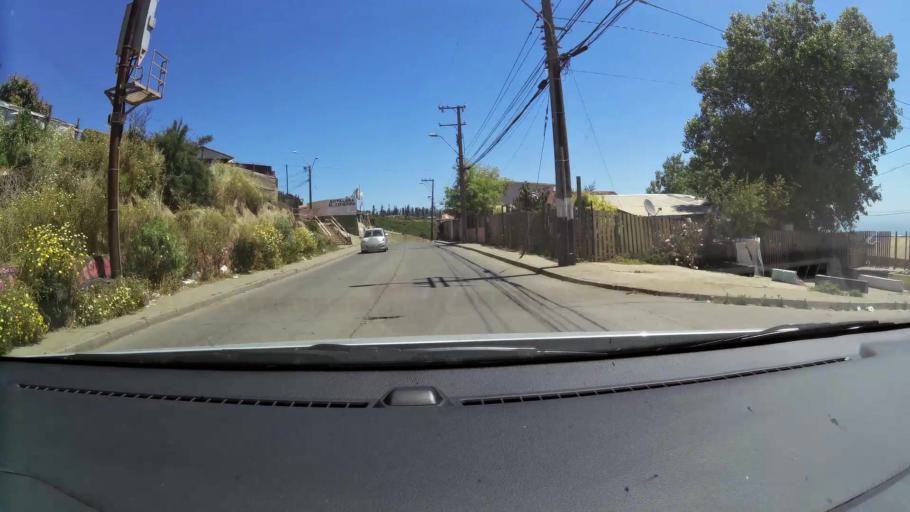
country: CL
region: Valparaiso
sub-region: Provincia de Valparaiso
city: Valparaiso
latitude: -33.0593
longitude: -71.6402
